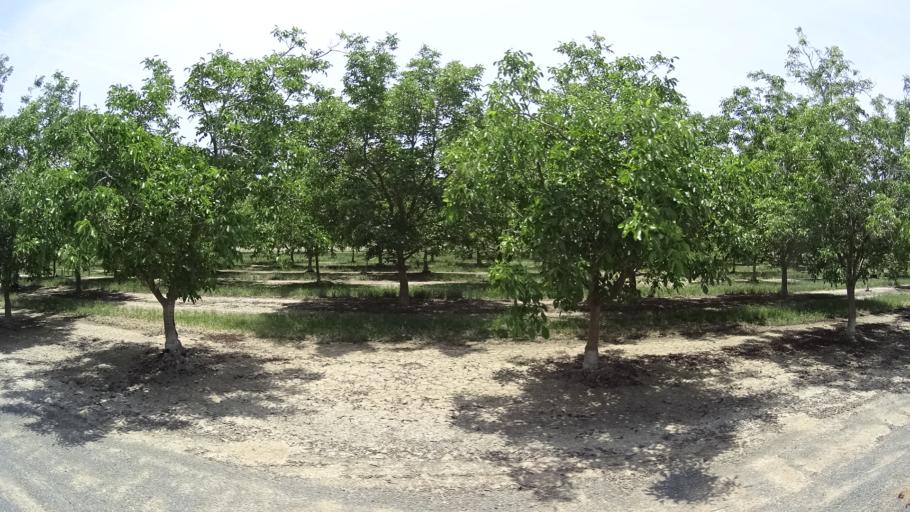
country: US
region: California
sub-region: Fresno County
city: Riverdale
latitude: 36.3947
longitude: -119.8620
